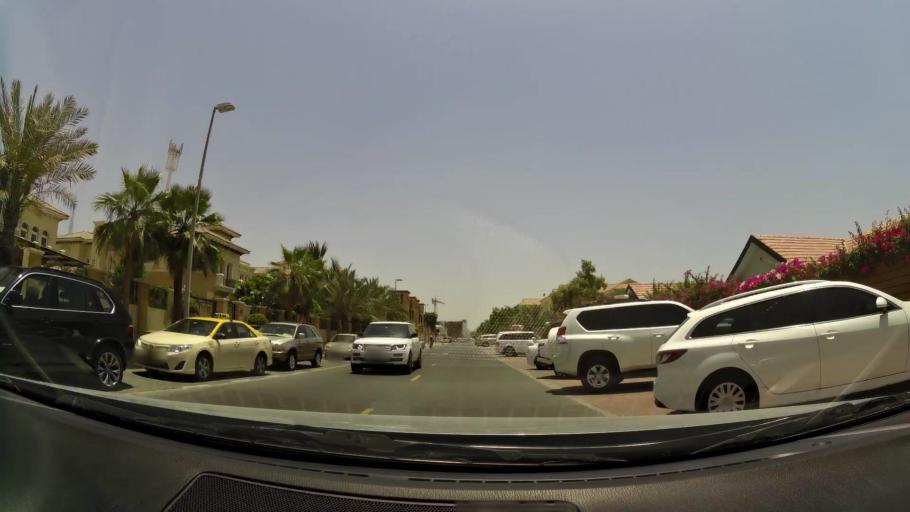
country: AE
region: Dubai
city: Dubai
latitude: 25.2236
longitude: 55.2624
